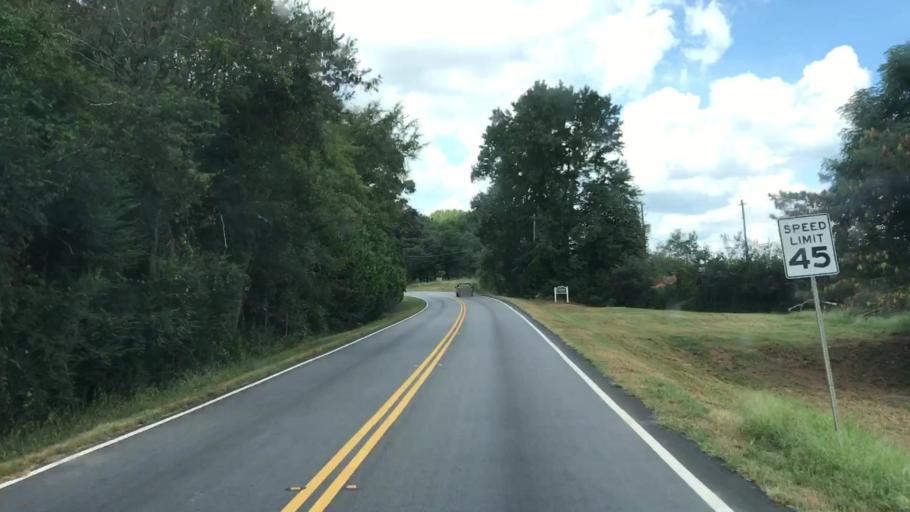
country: US
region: Georgia
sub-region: Greene County
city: Greensboro
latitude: 33.5713
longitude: -83.1672
